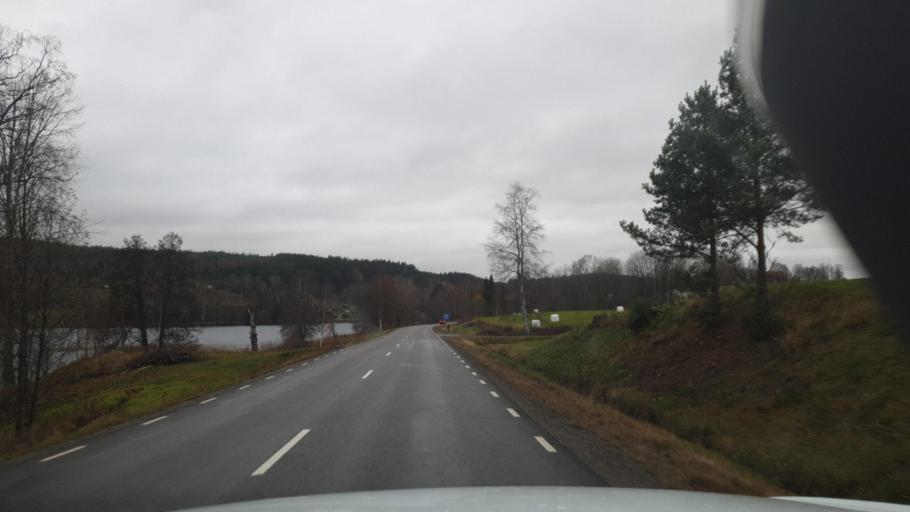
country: SE
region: Vaermland
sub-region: Eda Kommun
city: Amotfors
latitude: 59.8814
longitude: 12.5292
